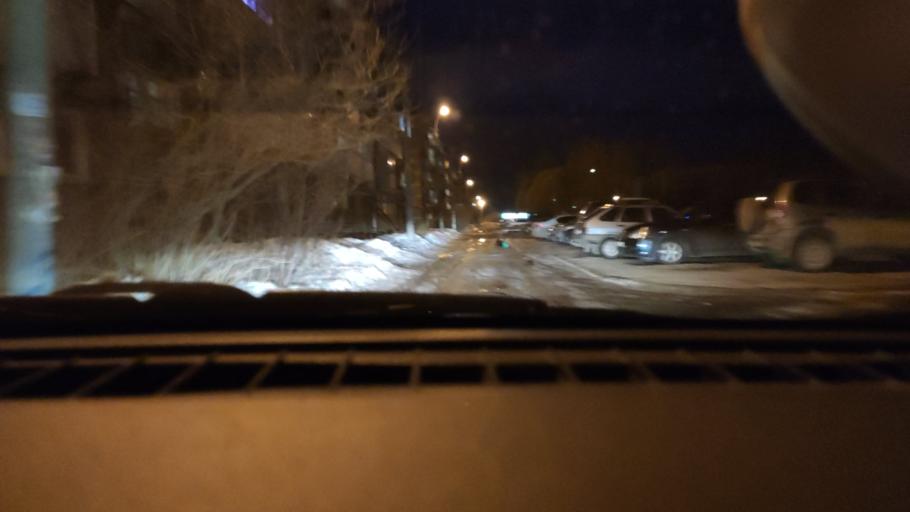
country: RU
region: Perm
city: Overyata
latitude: 58.0778
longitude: 55.8706
